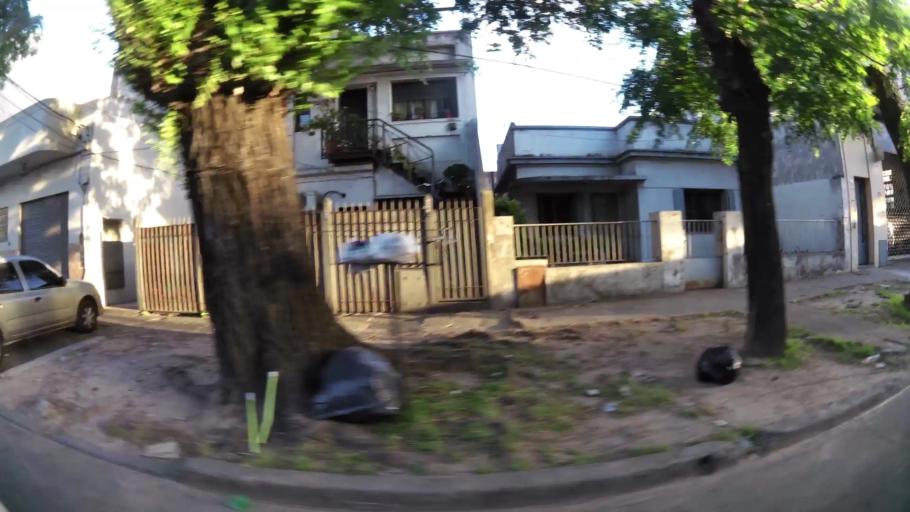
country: AR
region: Buenos Aires
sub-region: Partido de General San Martin
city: General San Martin
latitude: -34.5457
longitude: -58.4992
